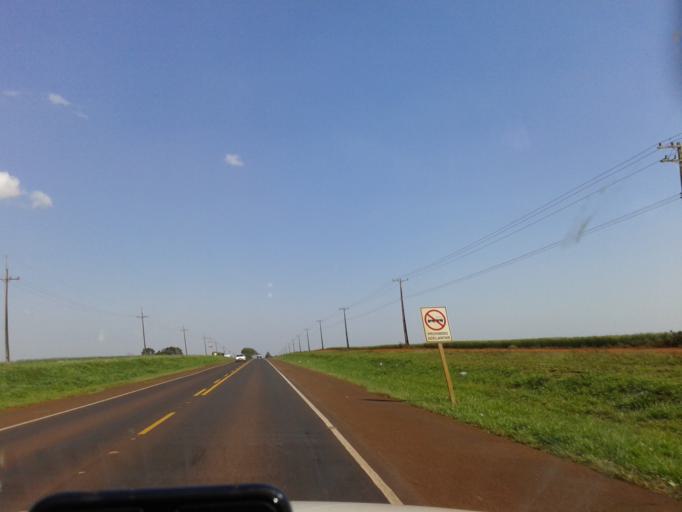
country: PY
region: Alto Parana
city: Santa Rita
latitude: -25.6974
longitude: -55.0181
